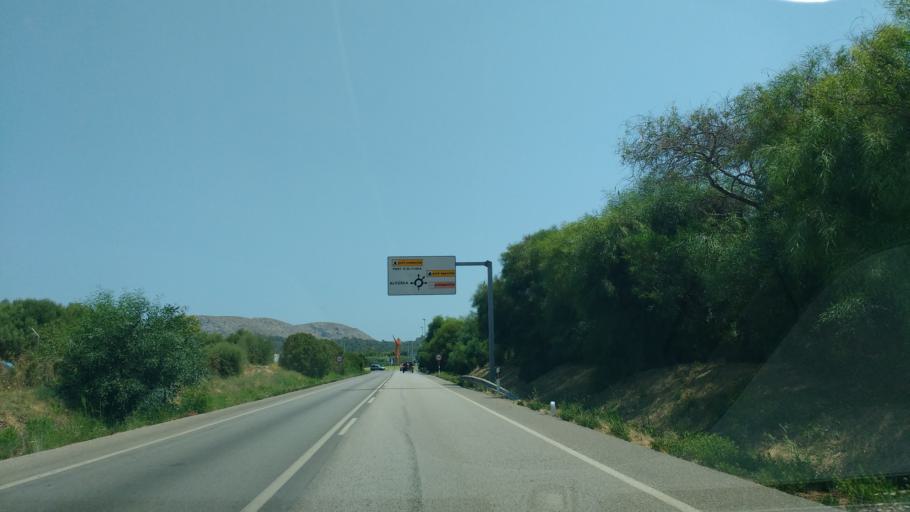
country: ES
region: Balearic Islands
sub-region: Illes Balears
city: Alcudia
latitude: 39.8459
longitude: 3.1220
